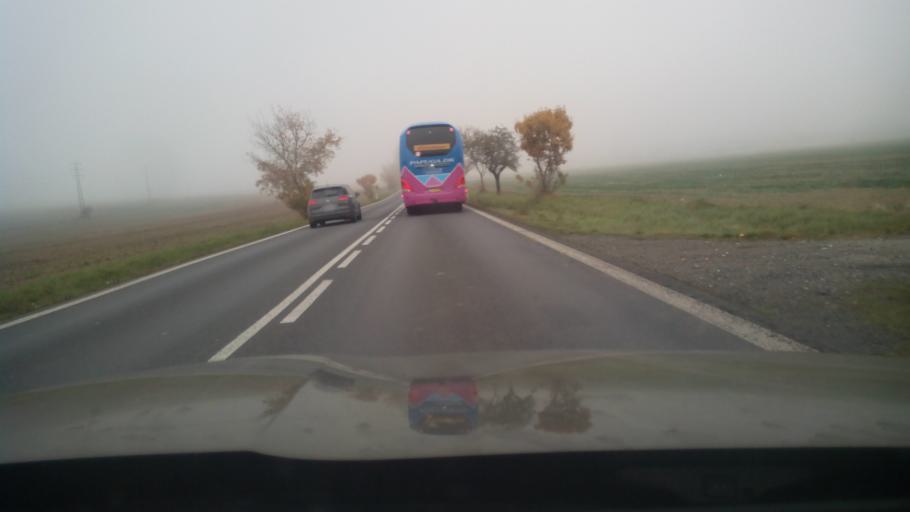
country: CZ
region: Jihocesky
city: Mirovice
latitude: 49.5609
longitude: 14.0787
